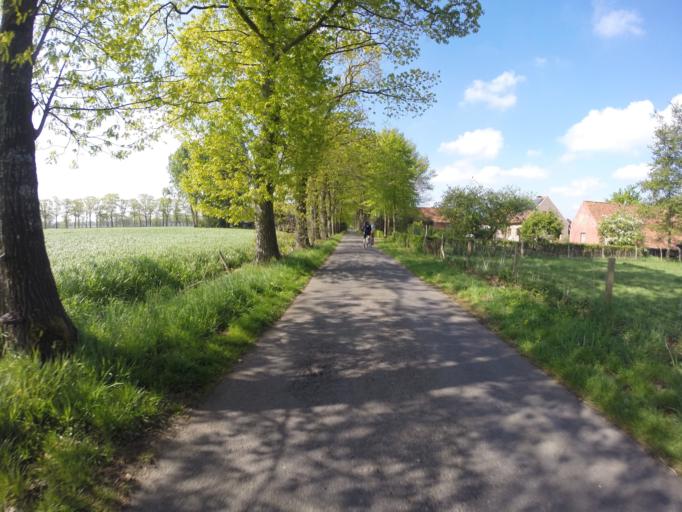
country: BE
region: Flanders
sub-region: Provincie West-Vlaanderen
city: Beernem
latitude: 51.1046
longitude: 3.3405
